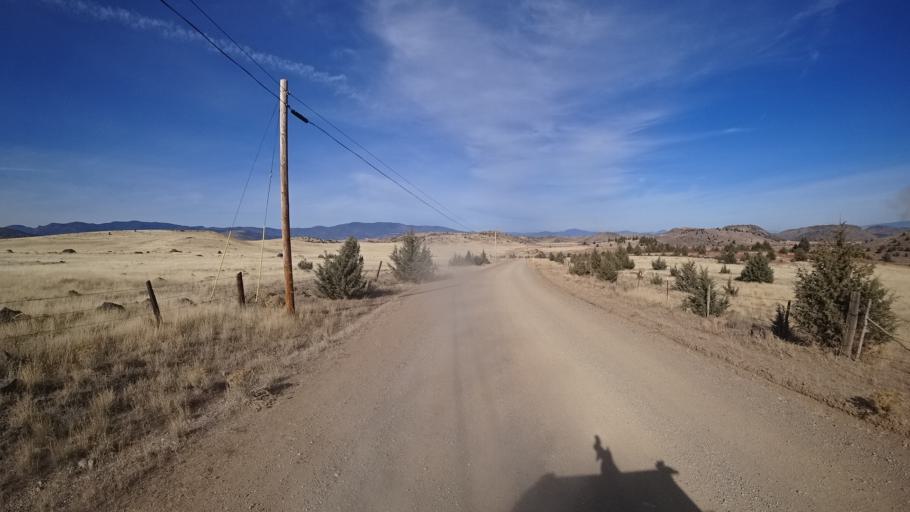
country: US
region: California
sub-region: Siskiyou County
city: Weed
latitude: 41.4913
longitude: -122.4514
